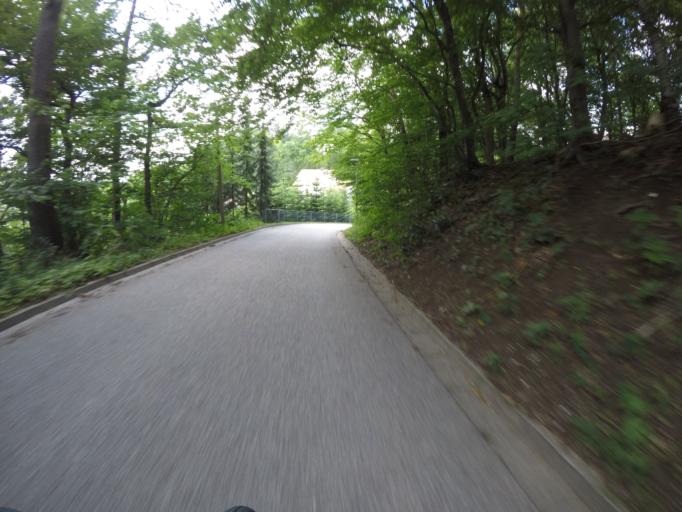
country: DE
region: Bavaria
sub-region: Lower Bavaria
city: Tiefenbach
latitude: 48.5030
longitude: 12.1032
